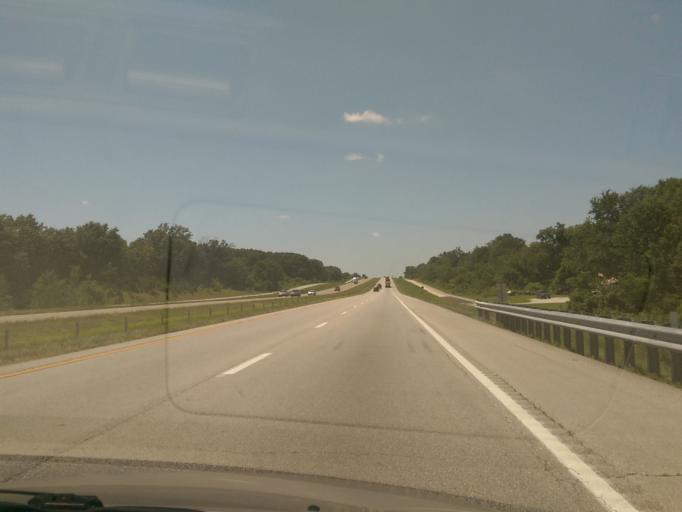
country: US
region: Missouri
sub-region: Cooper County
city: Boonville
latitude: 38.9353
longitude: -92.8743
